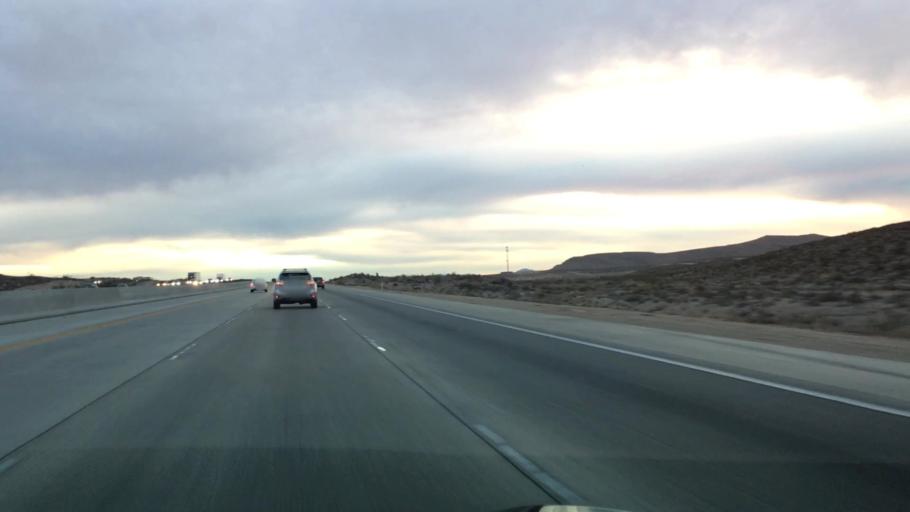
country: US
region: Nevada
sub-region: Clark County
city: Enterprise
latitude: 35.8964
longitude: -115.2174
